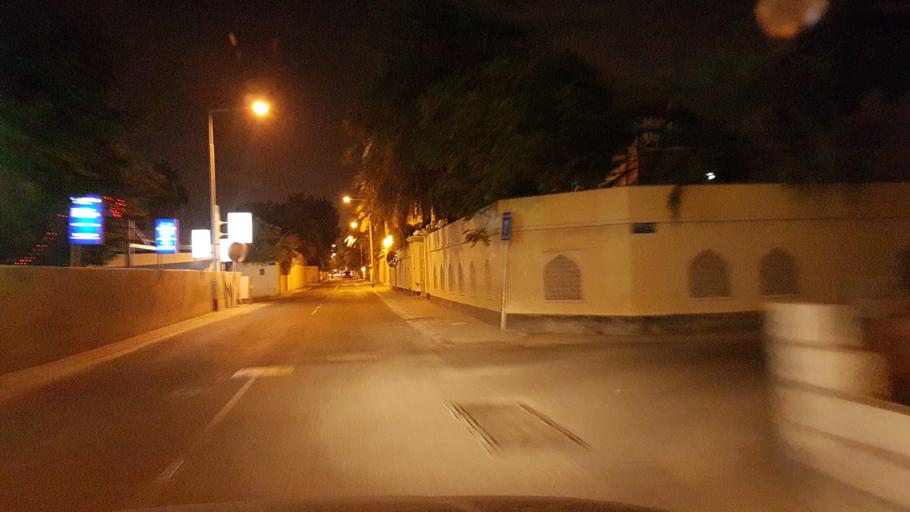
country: BH
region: Manama
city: Manama
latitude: 26.2192
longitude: 50.5829
